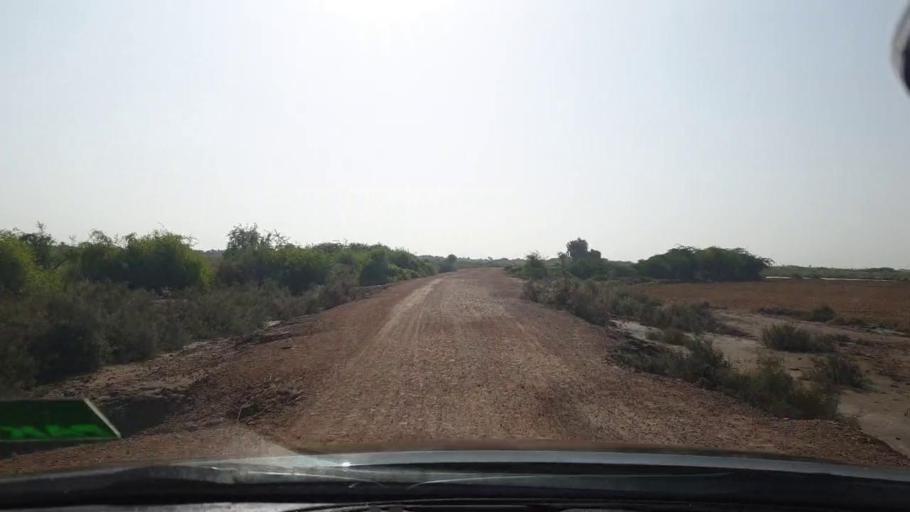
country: PK
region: Sindh
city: Tando Bago
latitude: 24.7177
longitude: 68.9678
